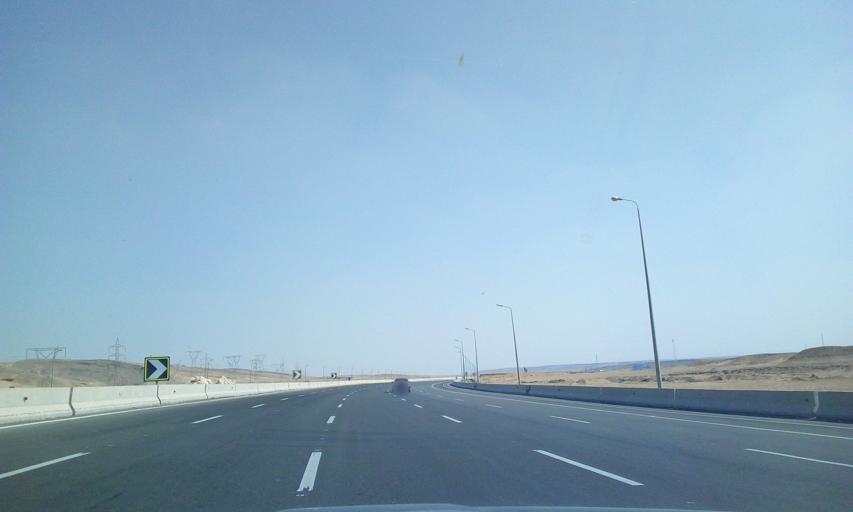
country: EG
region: As Suways
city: Ain Sukhna
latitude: 29.8200
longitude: 31.8923
